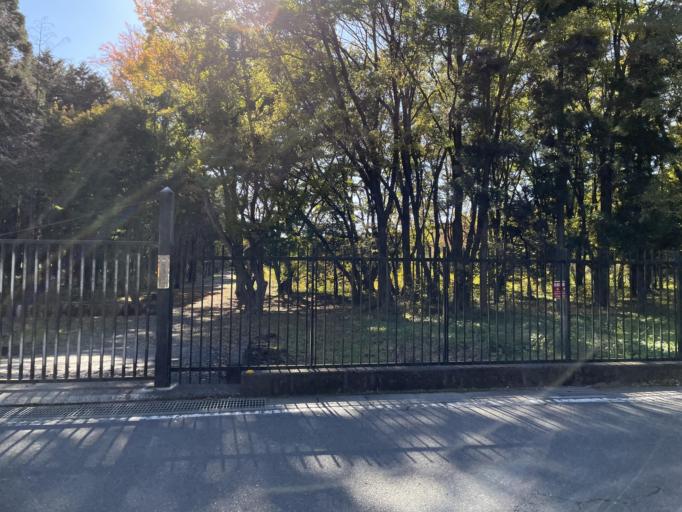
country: JP
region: Saitama
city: Asaka
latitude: 35.7952
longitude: 139.5626
